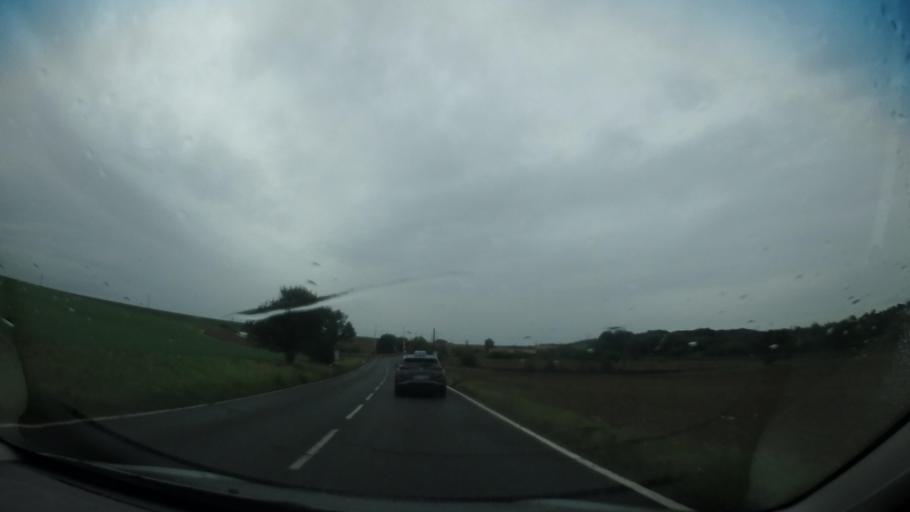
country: CZ
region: Central Bohemia
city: Milovice
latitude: 50.2223
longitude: 14.8765
